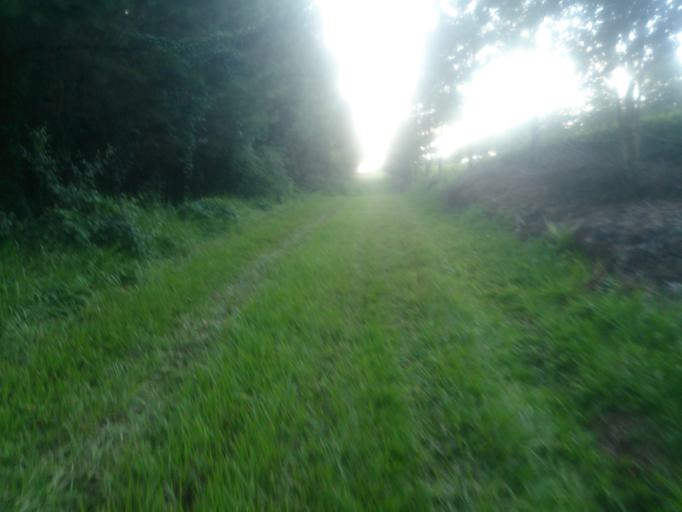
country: AR
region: Misiones
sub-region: Departamento de Obera
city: Obera
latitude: -27.4452
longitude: -55.0863
